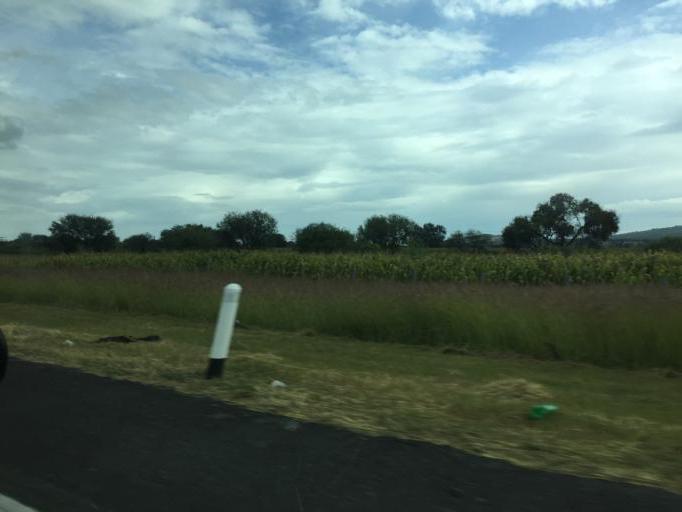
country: MX
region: Jalisco
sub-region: Ocotlan
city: Joconoxtle (La Tuna)
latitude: 20.3760
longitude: -102.6727
